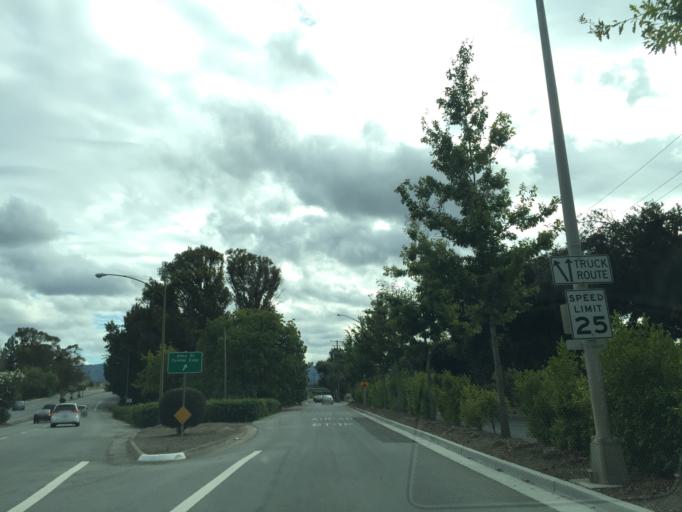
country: US
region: California
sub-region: Santa Clara County
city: Los Altos
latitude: 37.4111
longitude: -122.1069
